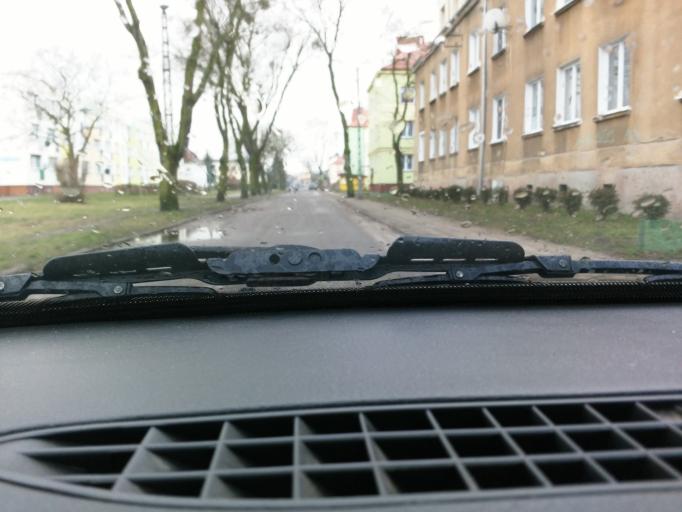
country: PL
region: Kujawsko-Pomorskie
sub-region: Grudziadz
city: Grudziadz
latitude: 53.4305
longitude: 18.7267
